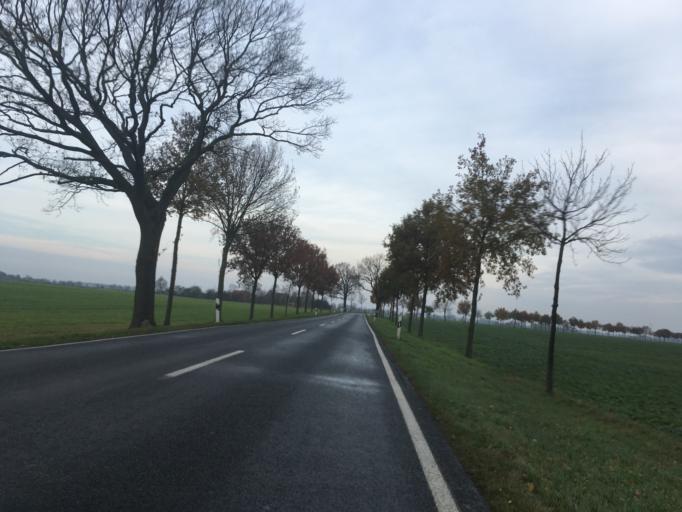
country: DE
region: Brandenburg
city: Letschin
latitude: 52.6053
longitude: 14.3454
